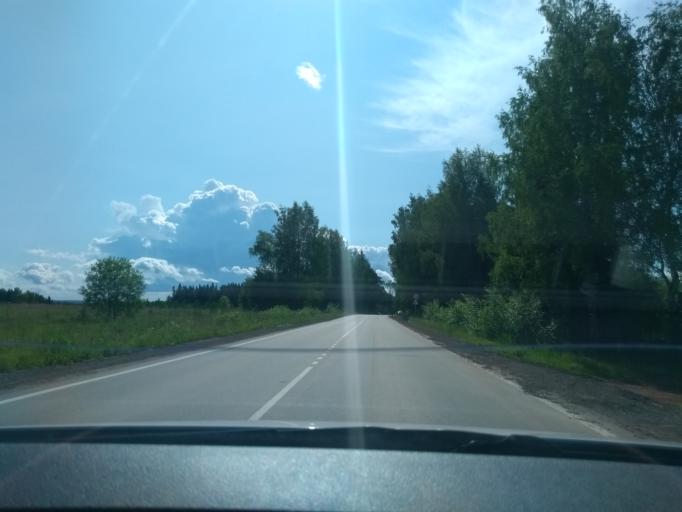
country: RU
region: Perm
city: Lobanovo
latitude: 57.8351
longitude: 56.3991
